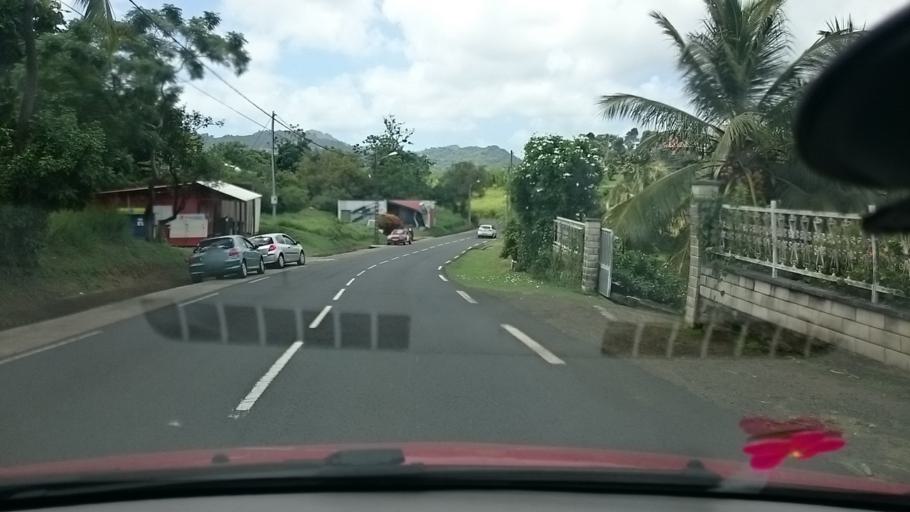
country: MQ
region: Martinique
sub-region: Martinique
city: Le Francois
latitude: 14.5979
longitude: -60.9292
